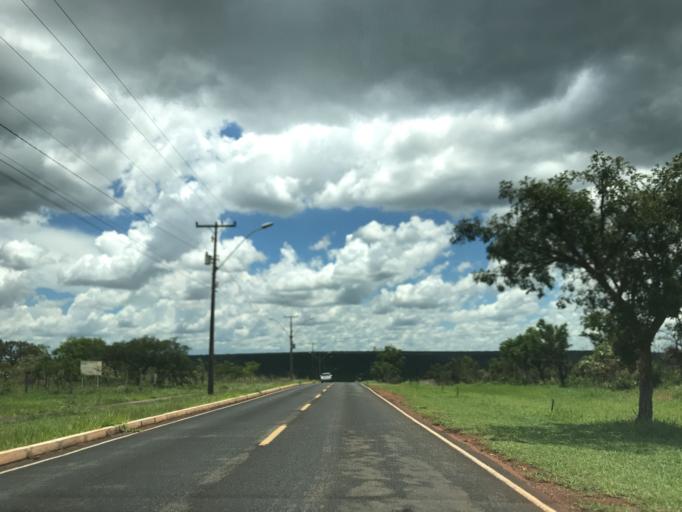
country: BR
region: Federal District
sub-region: Brasilia
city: Brasilia
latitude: -15.9008
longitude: -47.9188
